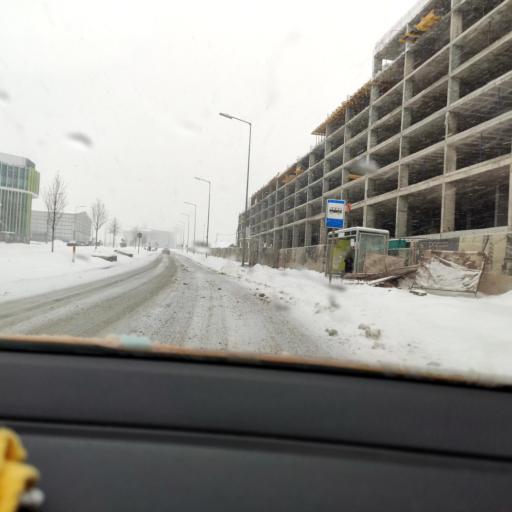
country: RU
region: Moskovskaya
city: Skolkovo
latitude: 55.6835
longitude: 37.3512
